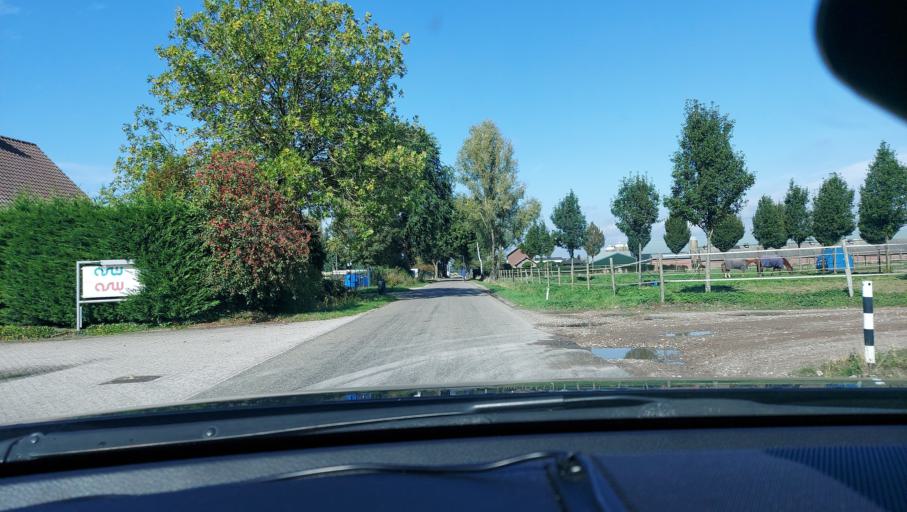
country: NL
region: Limburg
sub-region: Gemeente Nederweert
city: Nederweert
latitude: 51.3030
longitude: 5.7576
